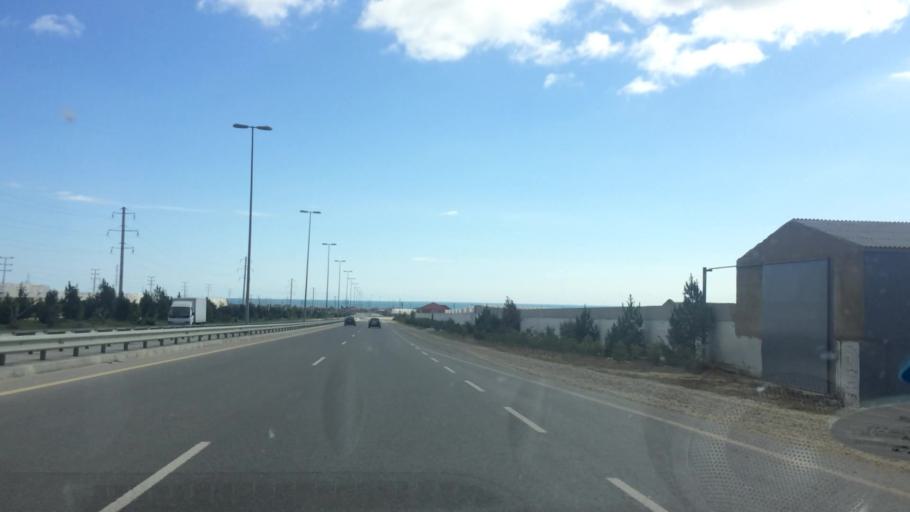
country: AZ
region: Baki
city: Zyrya
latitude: 40.4003
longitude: 50.3142
